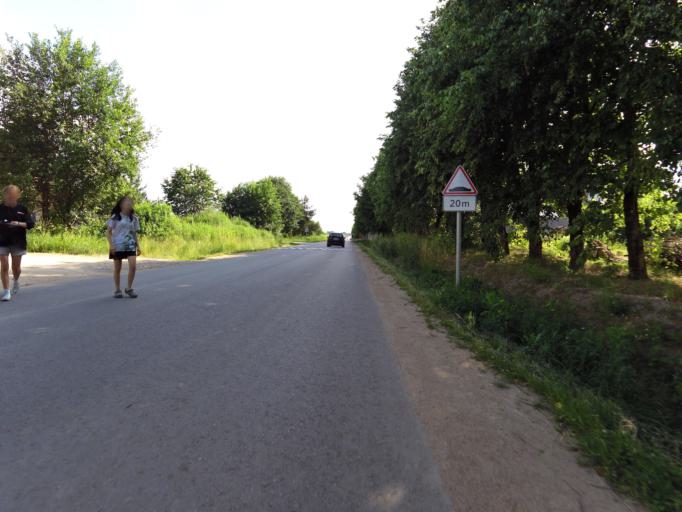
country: LT
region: Vilnius County
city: Pasilaiciai
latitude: 54.7628
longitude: 25.2253
